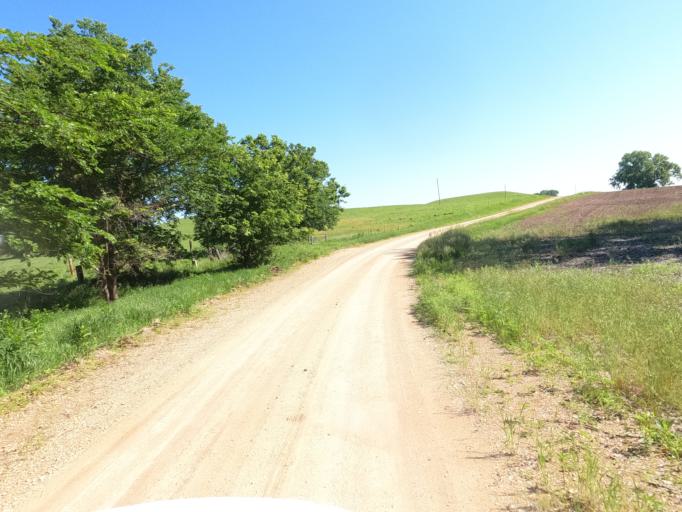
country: US
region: Kansas
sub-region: Marion County
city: Marion
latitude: 38.2550
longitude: -96.8591
